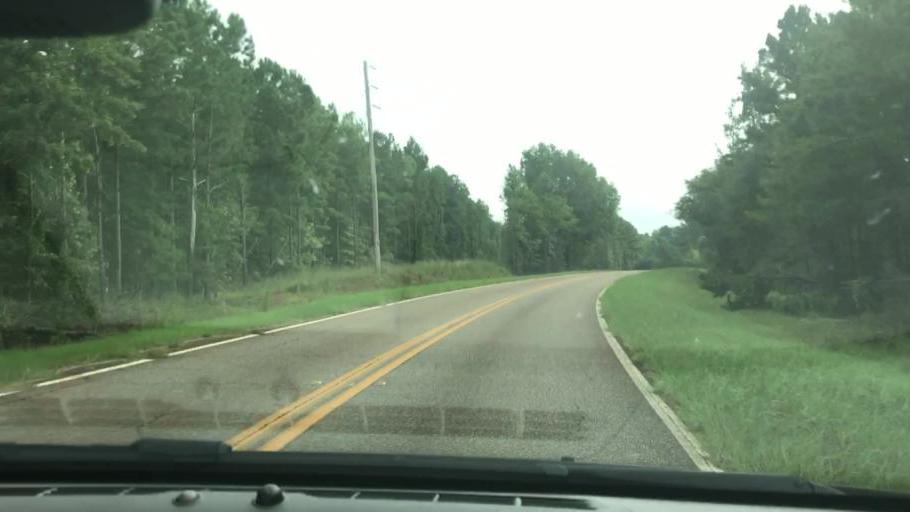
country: US
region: Georgia
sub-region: Stewart County
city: Lumpkin
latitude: 32.0484
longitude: -84.9053
